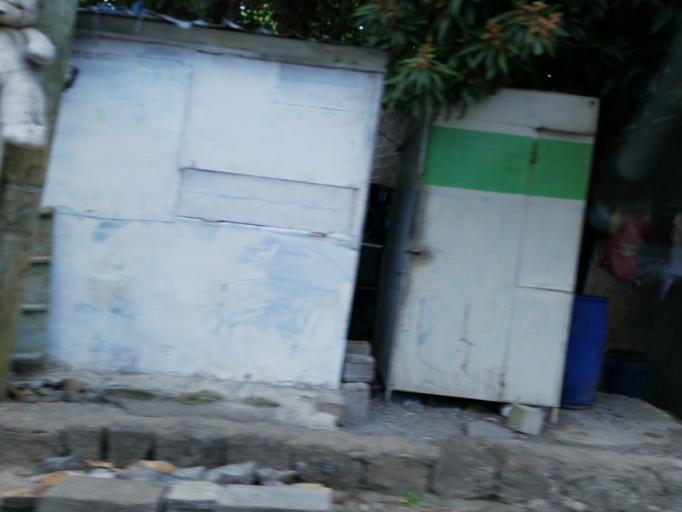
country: MU
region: Plaines Wilhems
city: Ebene
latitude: -20.2334
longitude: 57.4619
